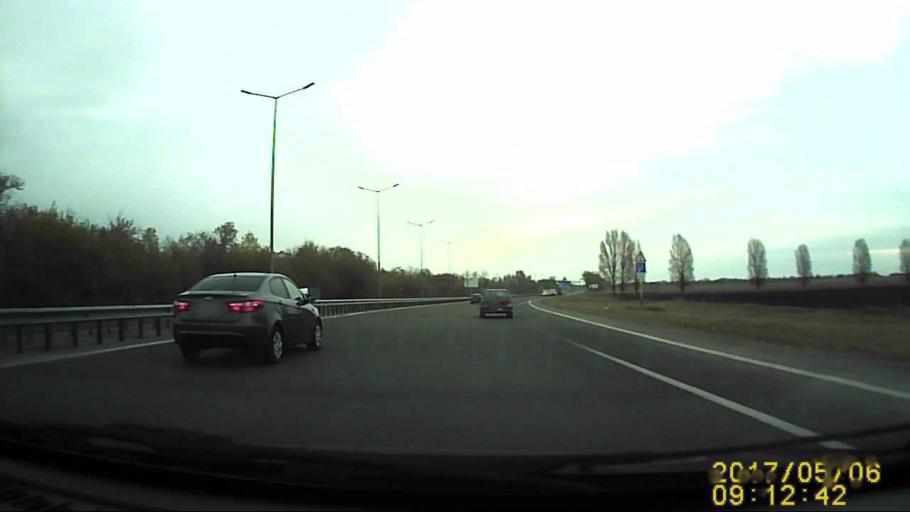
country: RU
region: Ulyanovsk
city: Mirnyy
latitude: 54.3602
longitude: 48.6787
